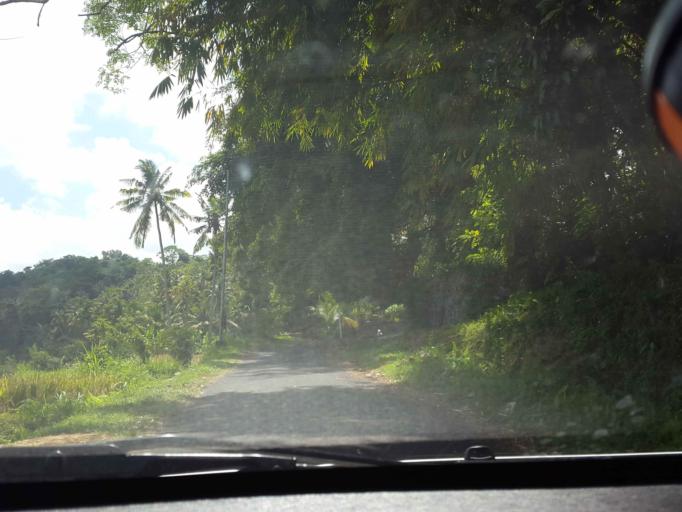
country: ID
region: Bali
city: Banjar Kelodan
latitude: -8.4995
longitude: 115.3942
